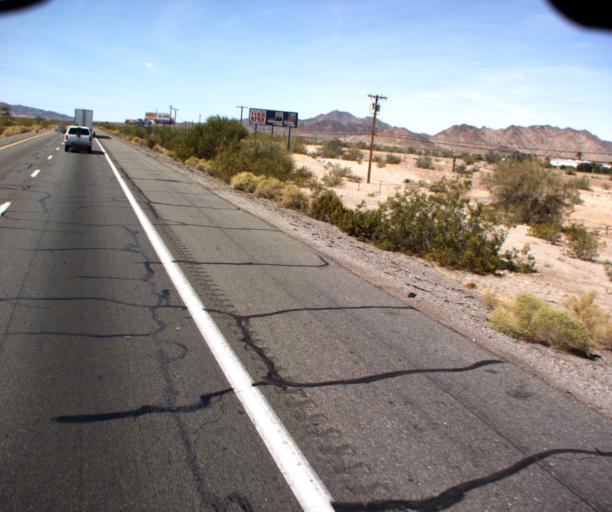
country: US
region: Arizona
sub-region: La Paz County
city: Quartzsite
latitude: 33.6589
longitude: -114.2479
